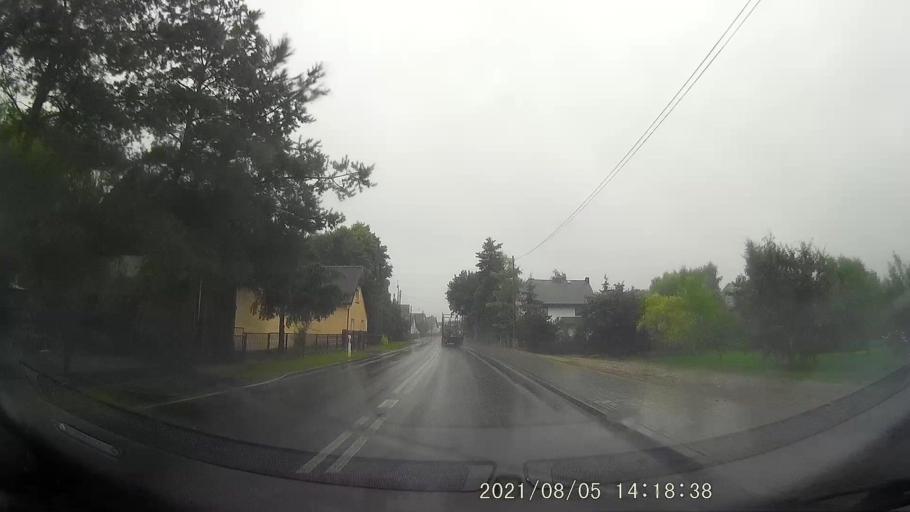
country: PL
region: Opole Voivodeship
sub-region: Powiat prudnicki
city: Biala
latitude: 50.4647
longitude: 17.6935
